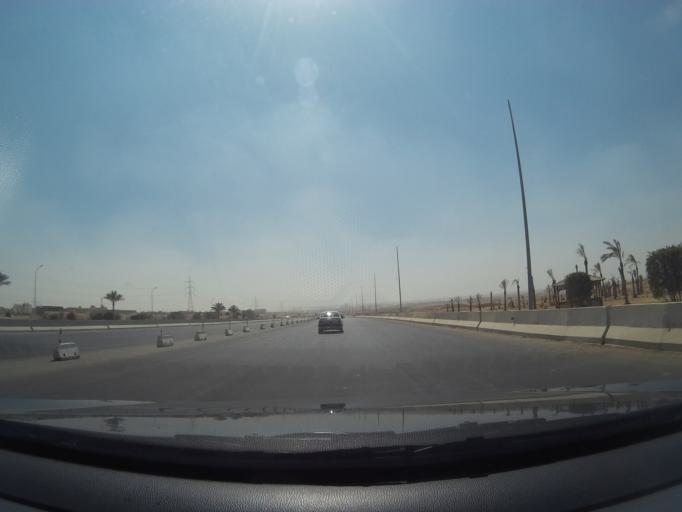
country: EG
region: As Suways
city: Ain Sukhna
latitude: 29.7631
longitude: 31.9624
